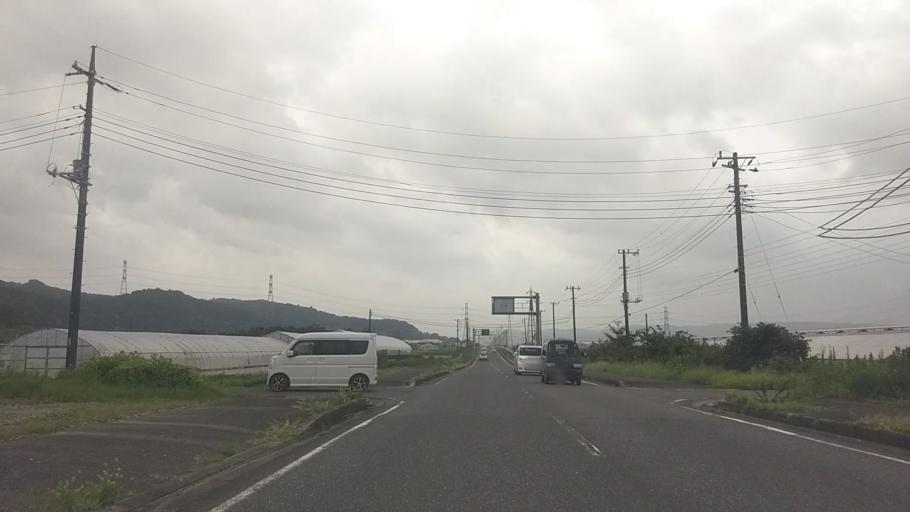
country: JP
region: Chiba
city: Kisarazu
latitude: 35.3540
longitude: 140.0548
